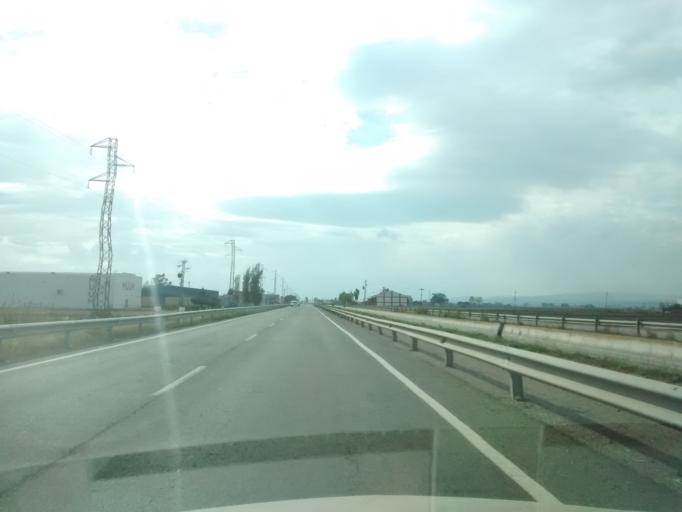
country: ES
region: Catalonia
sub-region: Provincia de Tarragona
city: Deltebre
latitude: 40.7257
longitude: 0.7143
